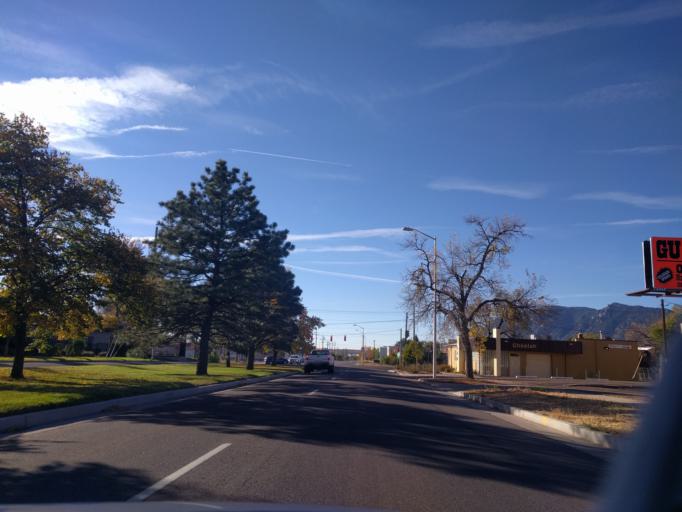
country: US
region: Colorado
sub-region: El Paso County
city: Colorado Springs
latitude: 38.8290
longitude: -104.8184
